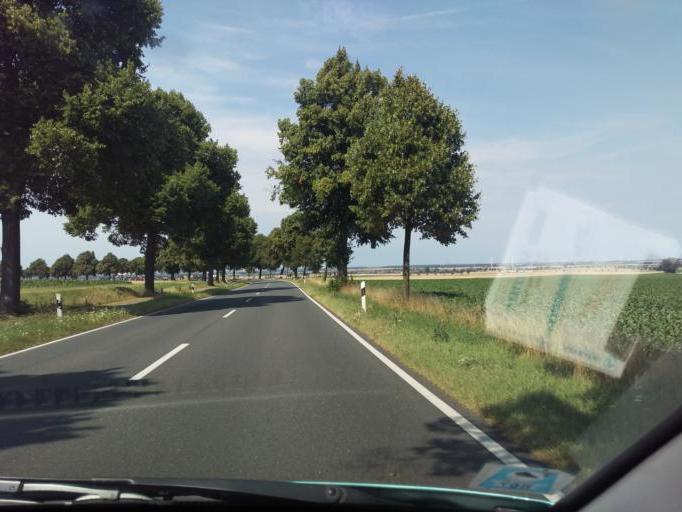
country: DE
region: Lower Saxony
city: Schellerten
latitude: 52.1370
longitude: 10.0349
